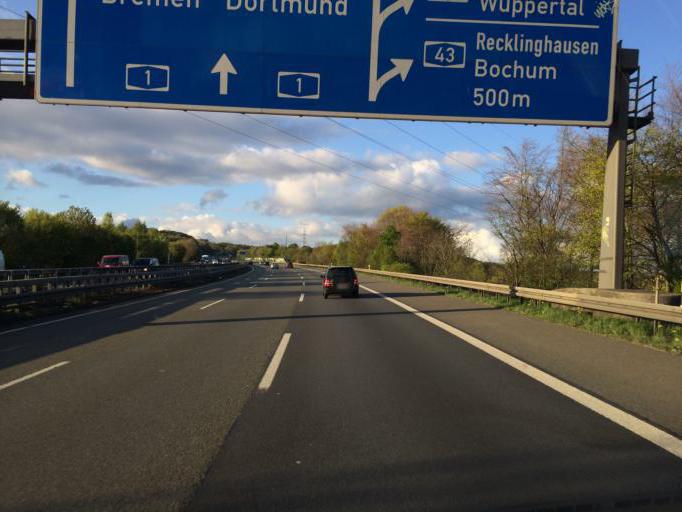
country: DE
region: North Rhine-Westphalia
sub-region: Regierungsbezirk Arnsberg
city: Schwelm
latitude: 51.2955
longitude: 7.2614
